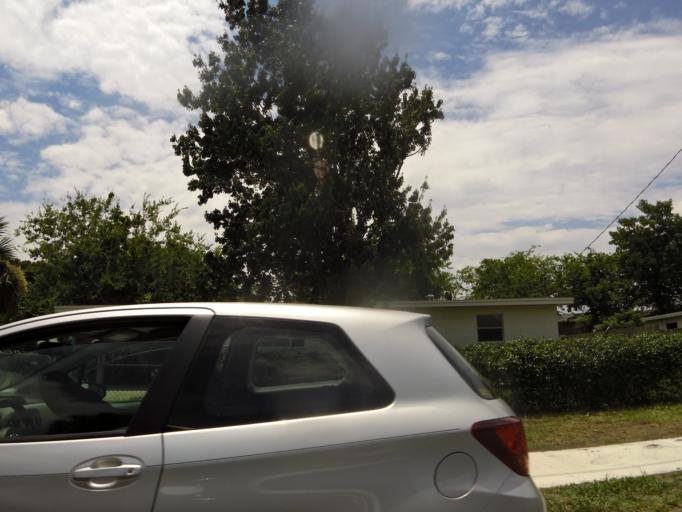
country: US
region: Florida
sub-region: Duval County
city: Atlantic Beach
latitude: 30.3315
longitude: -81.4127
